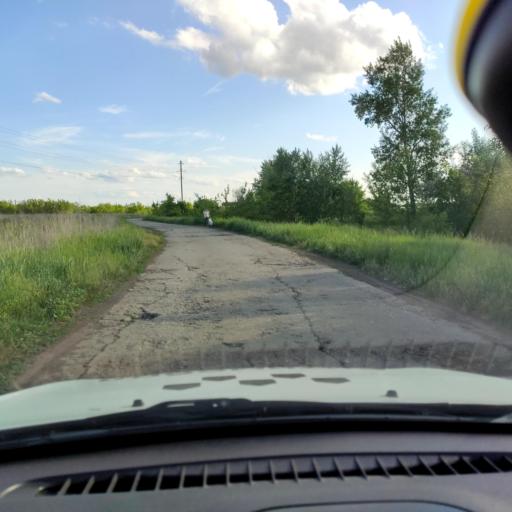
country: RU
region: Samara
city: Tol'yatti
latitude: 53.5953
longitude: 49.4571
